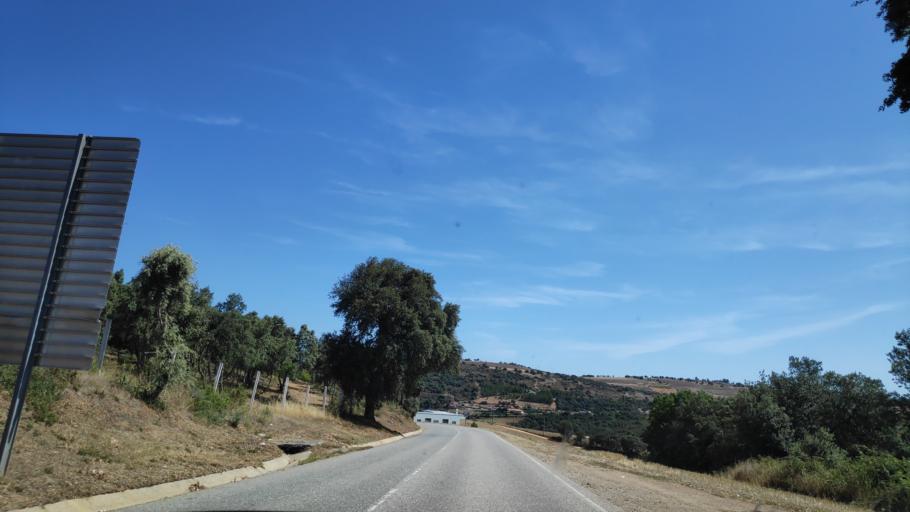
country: PT
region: Braganca
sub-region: Braganca Municipality
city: Braganca
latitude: 41.8237
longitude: -6.7510
